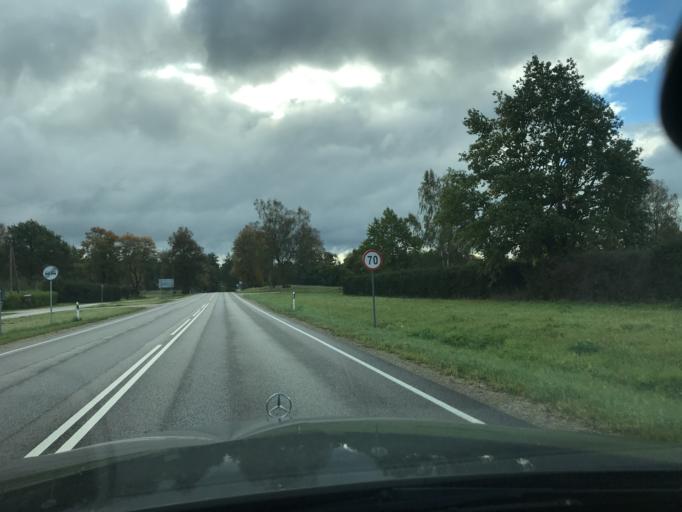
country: EE
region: Valgamaa
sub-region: Torva linn
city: Torva
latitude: 58.0200
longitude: 25.8738
